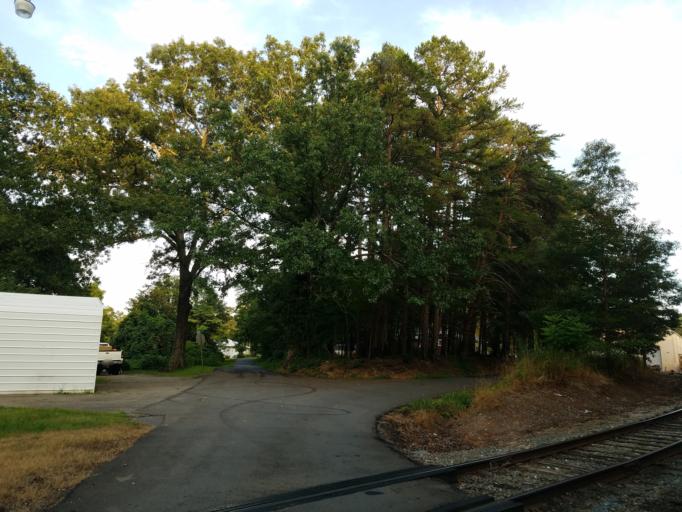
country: US
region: Georgia
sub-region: Pickens County
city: Nelson
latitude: 34.4168
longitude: -84.3882
